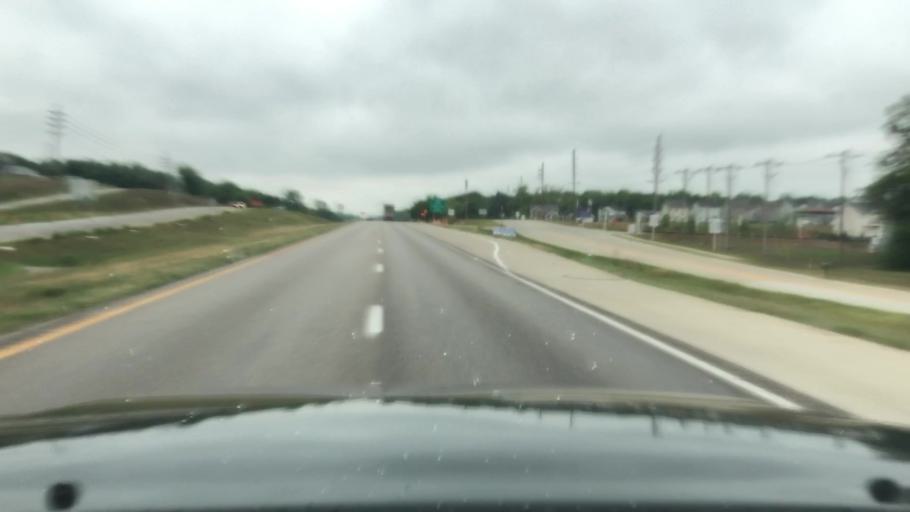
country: US
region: Missouri
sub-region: Saint Charles County
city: Wentzville
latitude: 38.8503
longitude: -90.8677
